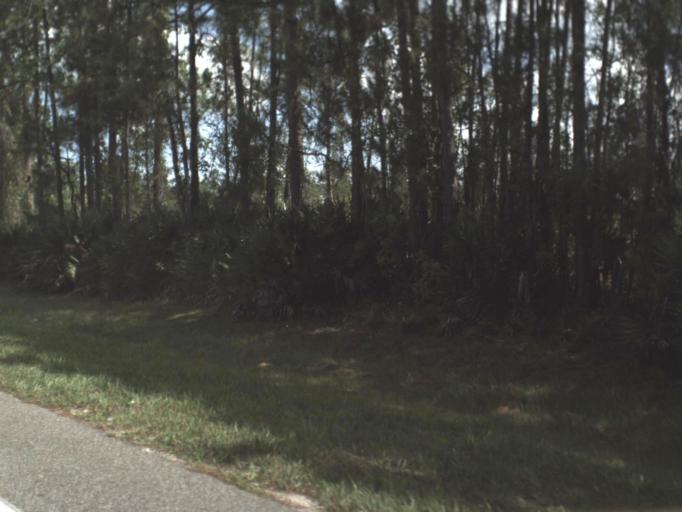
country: US
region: Florida
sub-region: Putnam County
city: East Palatka
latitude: 29.5809
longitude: -81.5584
